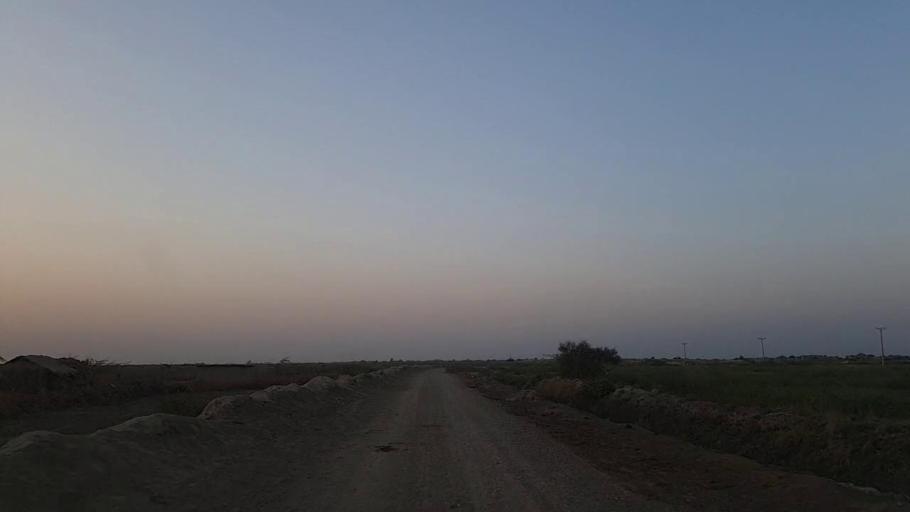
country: PK
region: Sindh
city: Naukot
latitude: 24.8961
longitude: 69.3588
